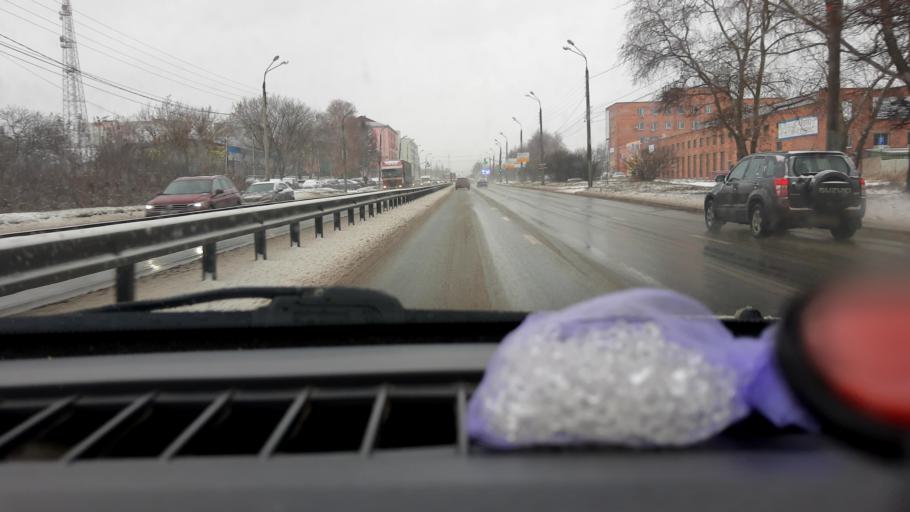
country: RU
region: Nizjnij Novgorod
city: Nizhniy Novgorod
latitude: 56.2401
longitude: 43.9857
